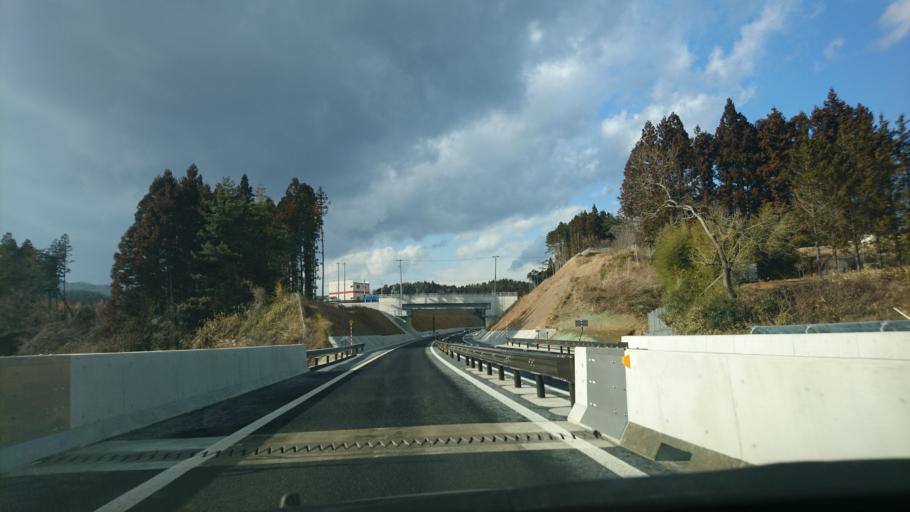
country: JP
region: Miyagi
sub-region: Oshika Gun
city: Onagawa Cho
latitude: 38.7614
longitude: 141.4997
